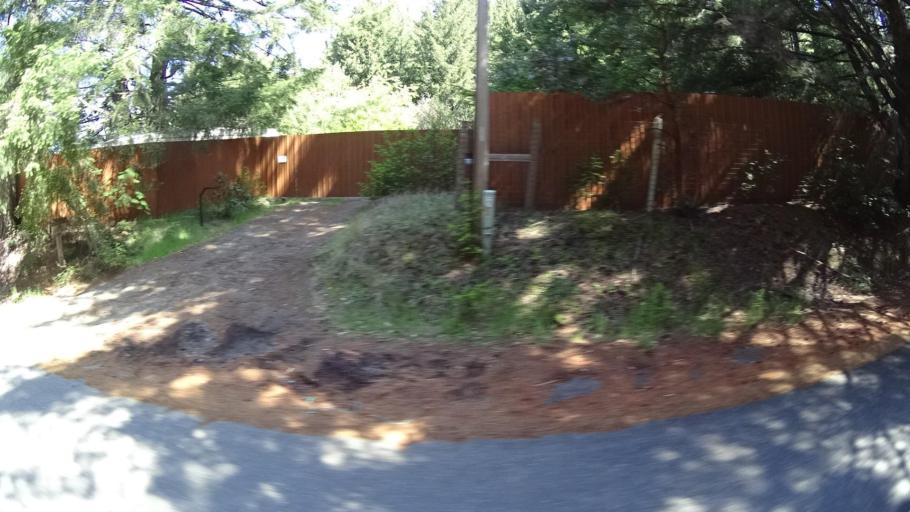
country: US
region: California
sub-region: Humboldt County
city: Redway
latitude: 40.1963
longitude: -124.0992
